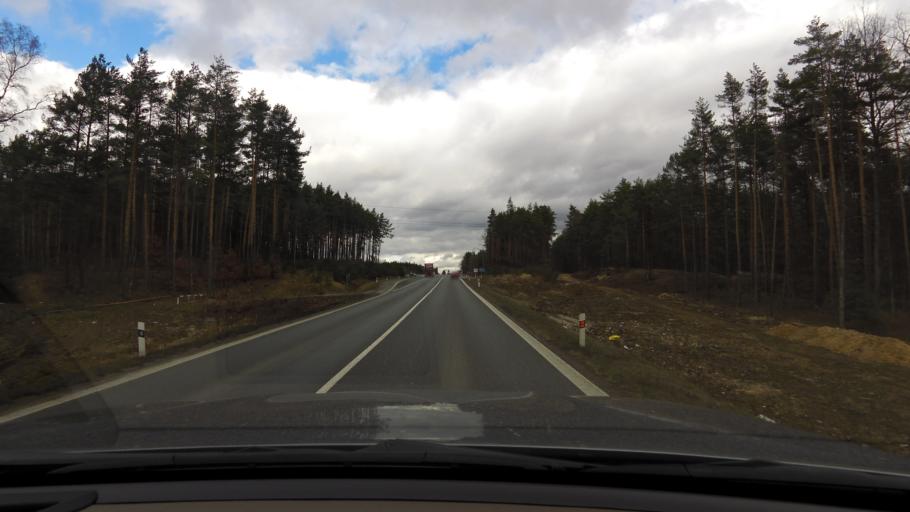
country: CZ
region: Plzensky
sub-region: Okres Plzen-Sever
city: Tremosna
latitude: 49.8003
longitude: 13.3875
